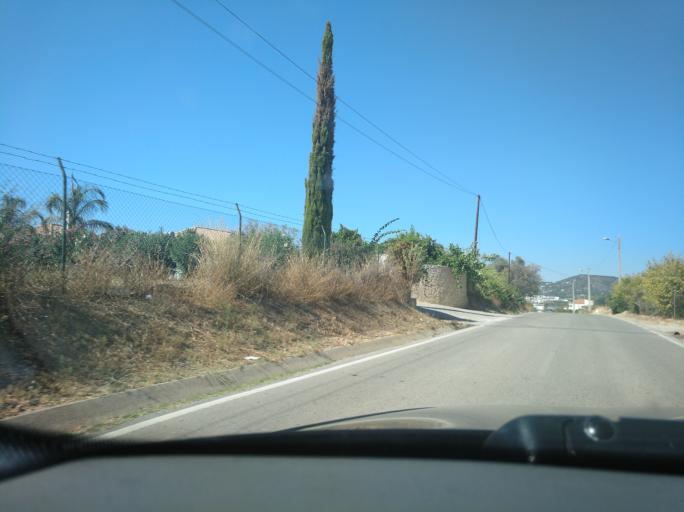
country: PT
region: Faro
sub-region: Faro
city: Faro
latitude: 37.0714
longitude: -7.8949
